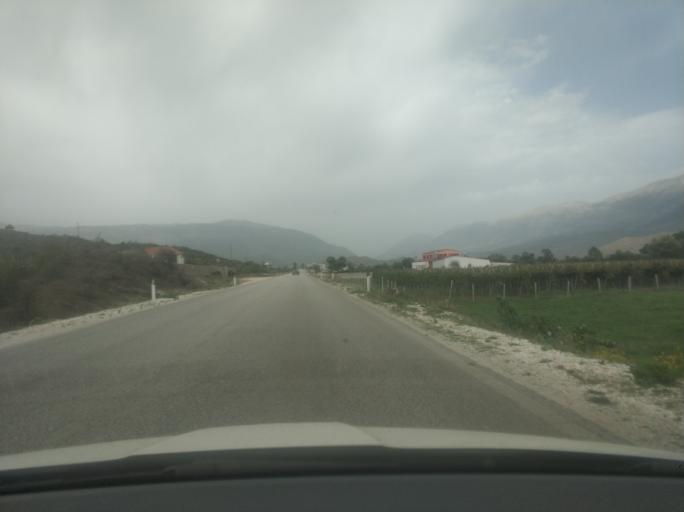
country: AL
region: Gjirokaster
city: Gjirokaster
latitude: 40.1102
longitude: 20.1217
